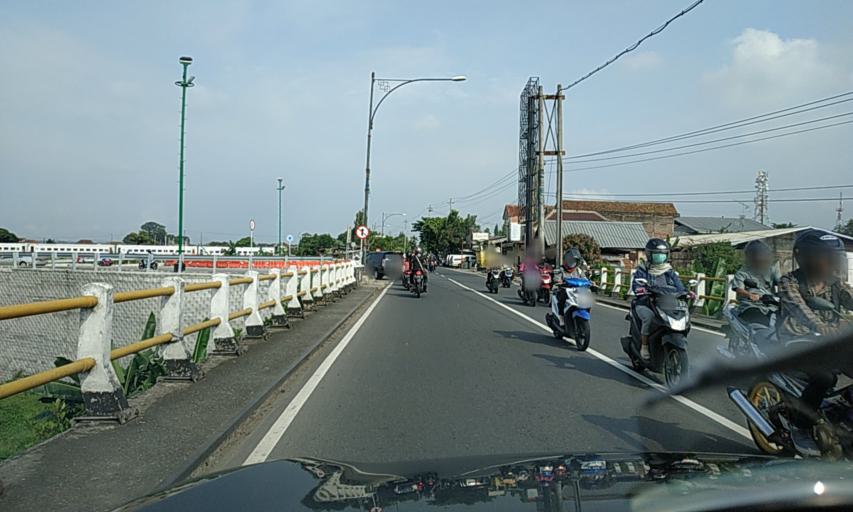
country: ID
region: Central Java
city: Purwokerto
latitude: -7.4239
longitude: 109.2241
